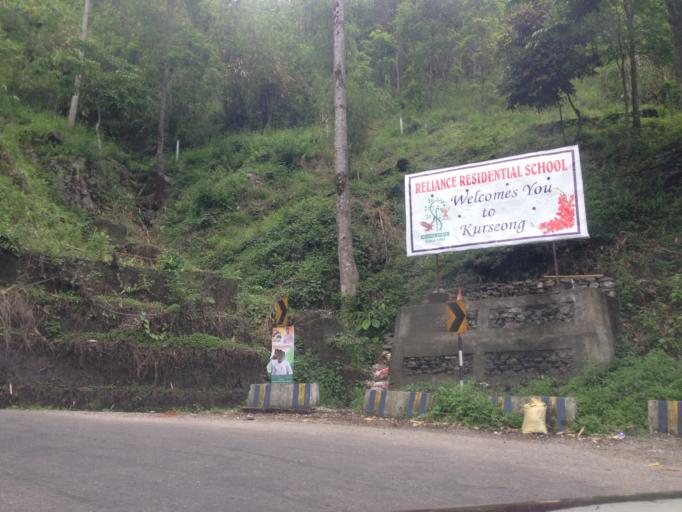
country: IN
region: West Bengal
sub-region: Darjiling
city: Karsiyang
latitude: 26.8583
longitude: 88.2968
